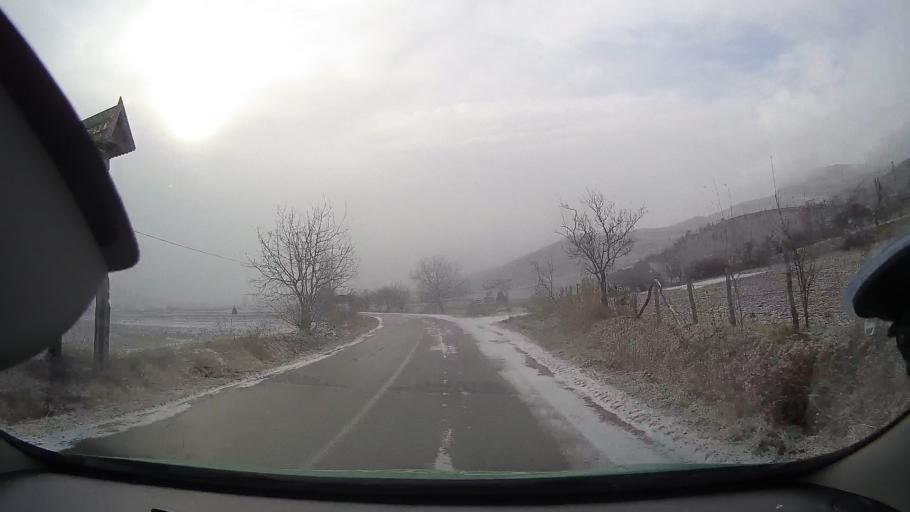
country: RO
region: Alba
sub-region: Comuna Rimetea
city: Rimetea
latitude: 46.4170
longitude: 23.5583
